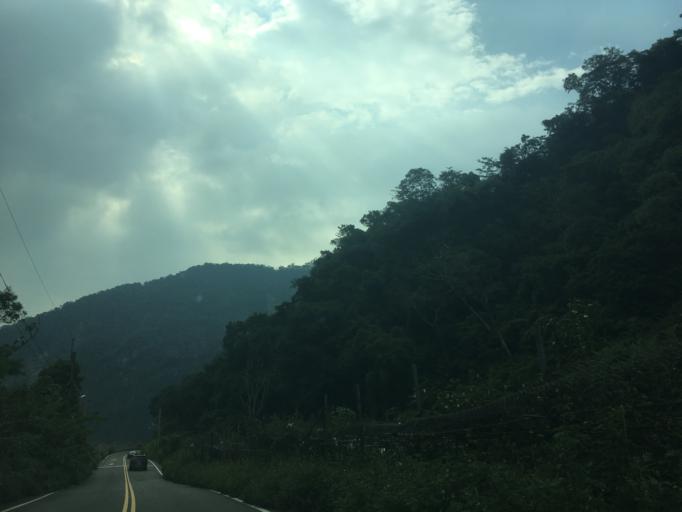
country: TW
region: Taiwan
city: Fengyuan
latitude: 24.2979
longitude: 120.9245
